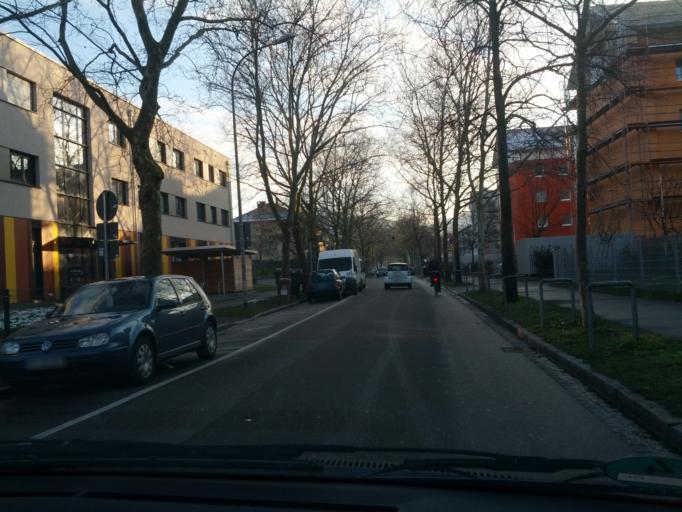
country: DE
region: Baden-Wuerttemberg
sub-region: Freiburg Region
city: Merzhausen
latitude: 47.9898
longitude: 7.8199
